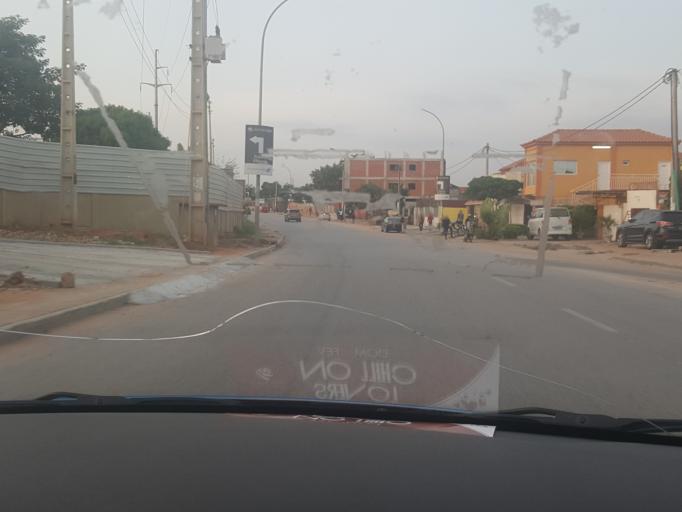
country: AO
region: Luanda
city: Luanda
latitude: -8.9137
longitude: 13.2017
